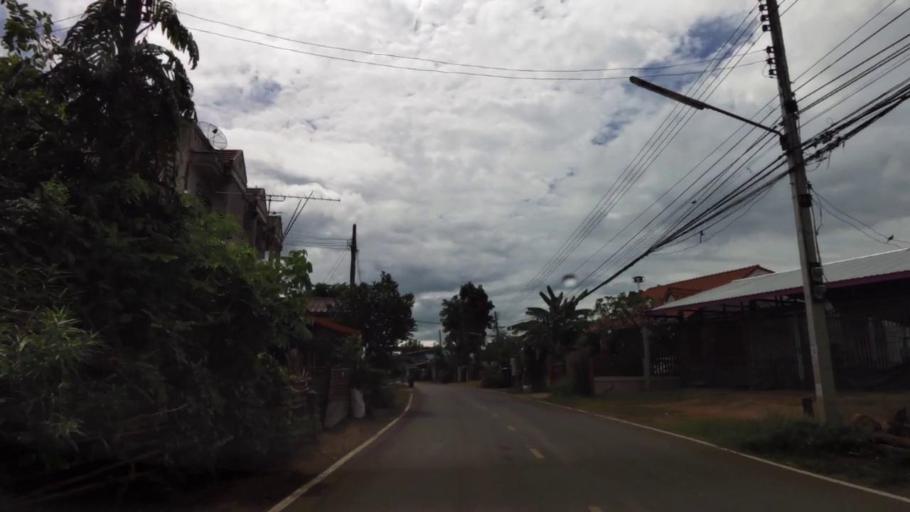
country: TH
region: Nakhon Sawan
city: Phai Sali
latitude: 15.5973
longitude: 100.6453
